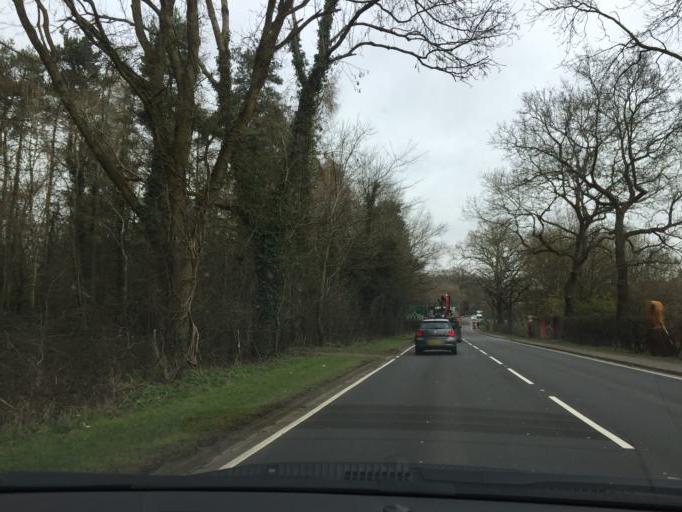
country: GB
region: England
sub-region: Warwickshire
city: Studley
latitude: 52.2953
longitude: -1.8813
